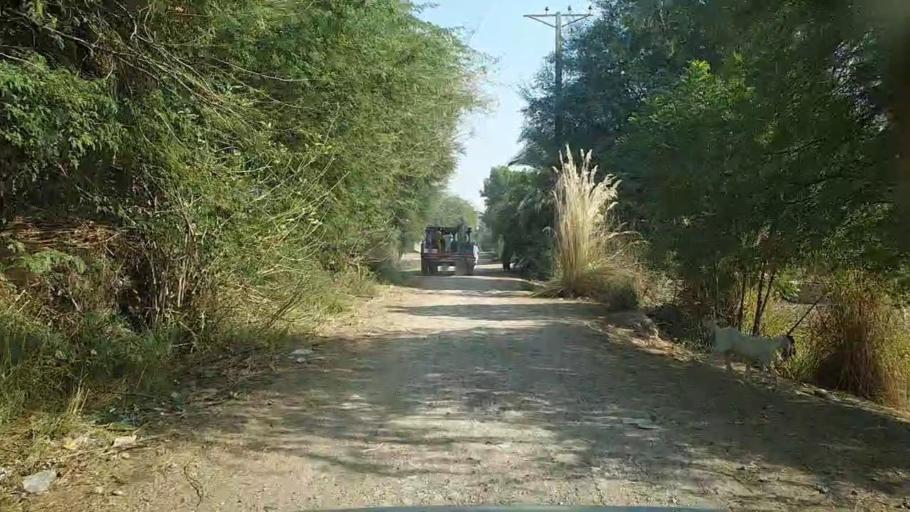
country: PK
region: Sindh
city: Kandiari
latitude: 26.9410
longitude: 68.5389
